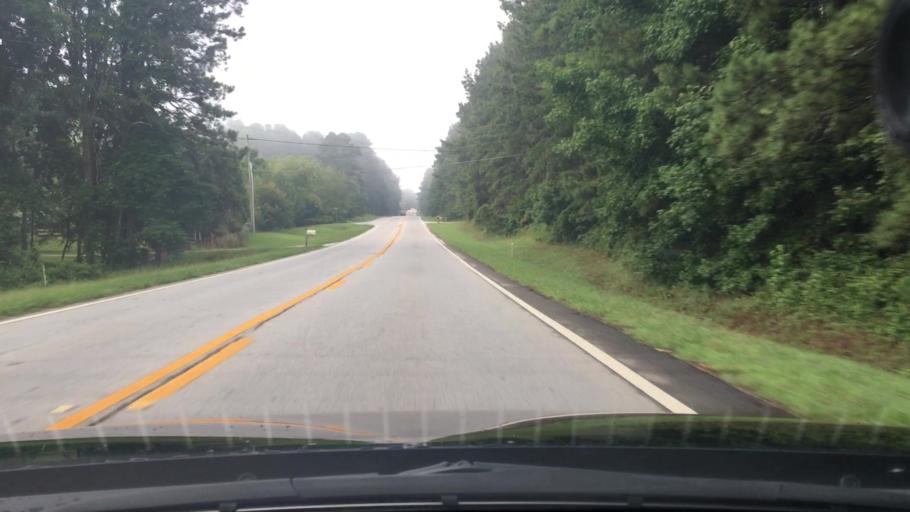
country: US
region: Georgia
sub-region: Fayette County
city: Peachtree City
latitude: 33.3748
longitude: -84.6272
